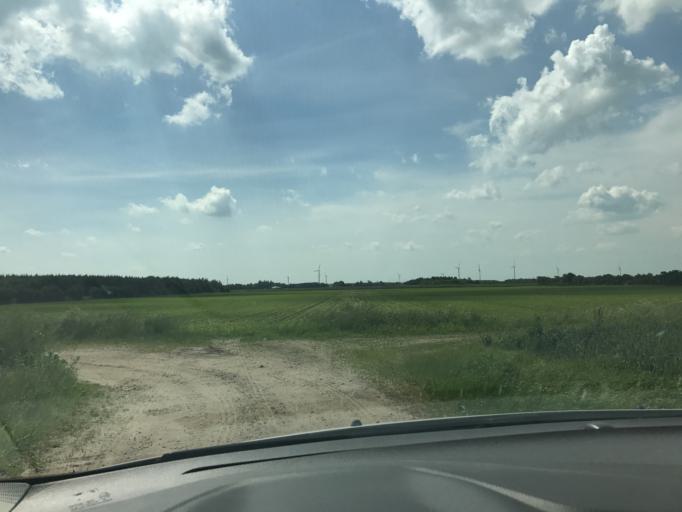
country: DE
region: Schleswig-Holstein
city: Ellhoft
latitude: 54.9287
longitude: 8.9513
